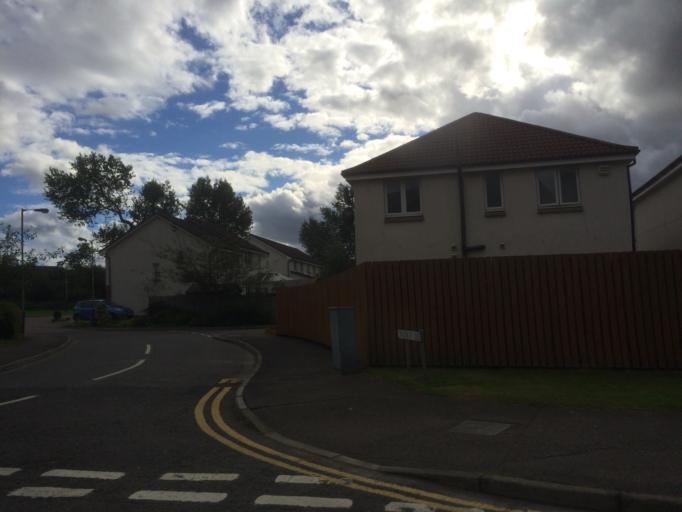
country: GB
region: Scotland
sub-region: Perth and Kinross
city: Luncarty
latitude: 56.4146
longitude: -3.4689
